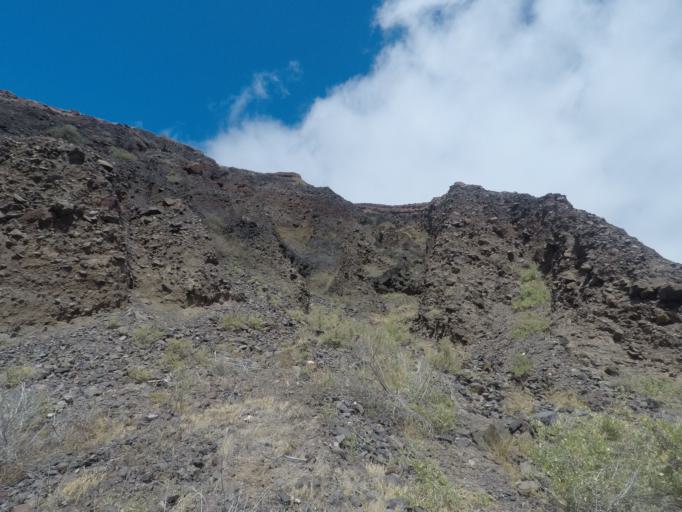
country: PT
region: Madeira
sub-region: Porto Santo
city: Vila de Porto Santo
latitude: 33.0617
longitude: -16.3016
